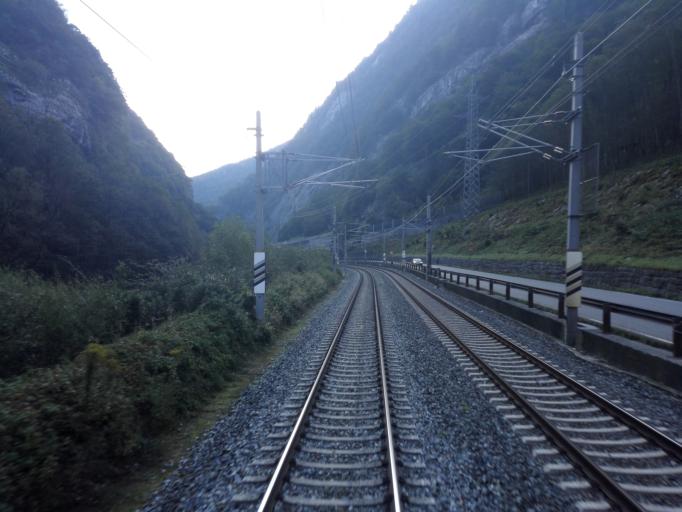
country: AT
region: Salzburg
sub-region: Politischer Bezirk Hallein
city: Golling an der Salzach
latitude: 47.5660
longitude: 13.1775
